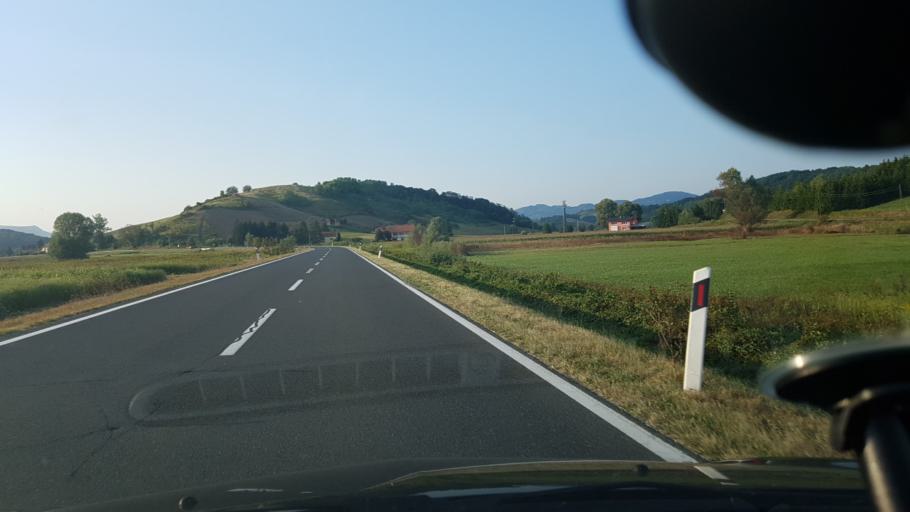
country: HR
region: Krapinsko-Zagorska
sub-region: Grad Krapina
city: Krapina
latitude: 46.1098
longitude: 15.8136
